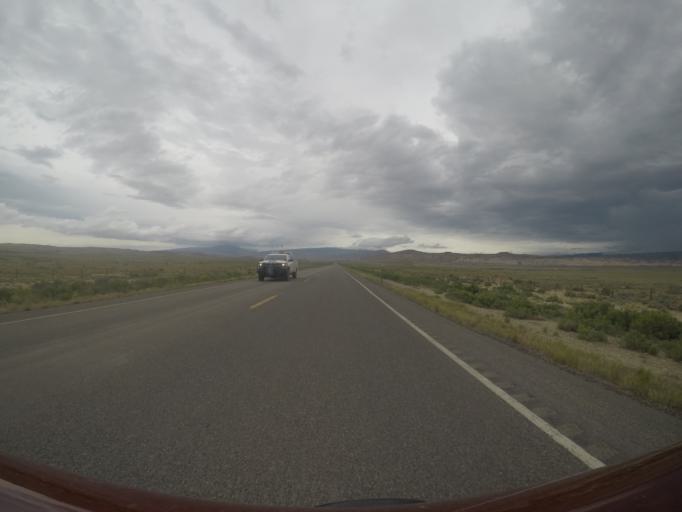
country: US
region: Wyoming
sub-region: Big Horn County
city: Lovell
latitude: 44.8951
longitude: -108.2891
